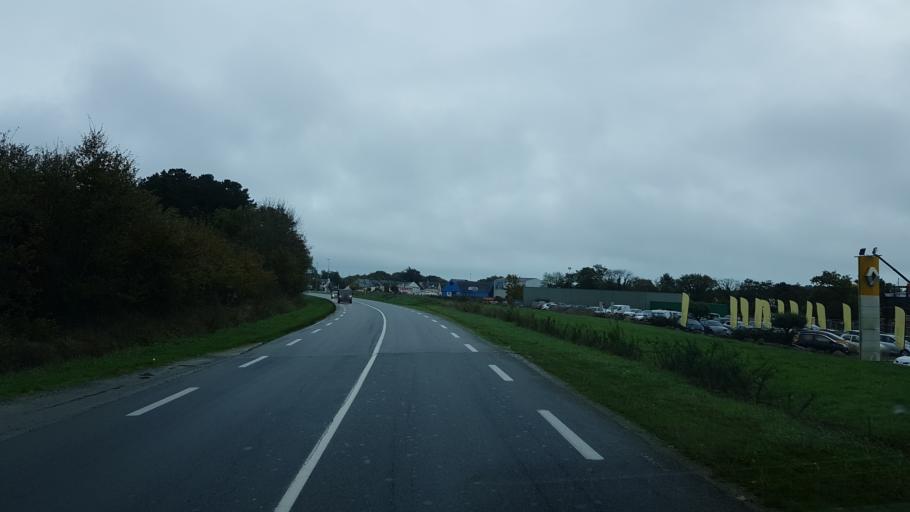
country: FR
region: Brittany
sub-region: Departement du Morbihan
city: Sarzeau
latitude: 47.5224
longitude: -2.7832
